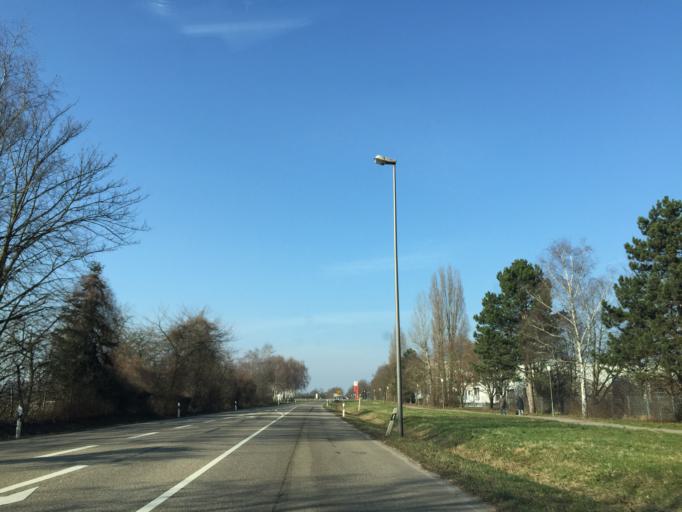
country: DE
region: Baden-Wuerttemberg
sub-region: Karlsruhe Region
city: Eppelheim
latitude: 49.4214
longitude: 8.6401
